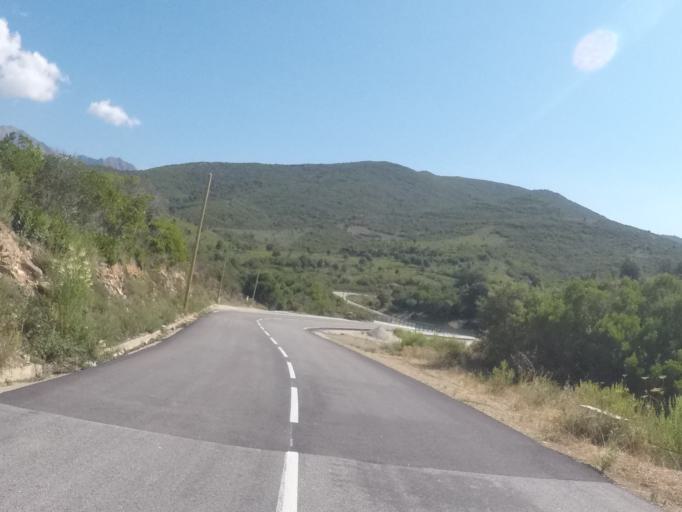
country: FR
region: Corsica
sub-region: Departement de la Haute-Corse
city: Calvi
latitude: 42.4299
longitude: 8.7325
